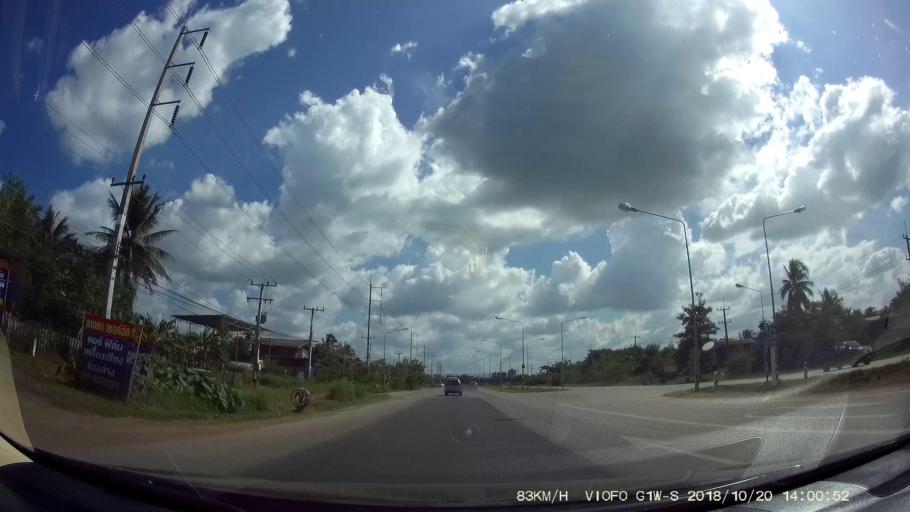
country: TH
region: Khon Kaen
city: Chum Phae
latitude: 16.5088
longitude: 102.1187
